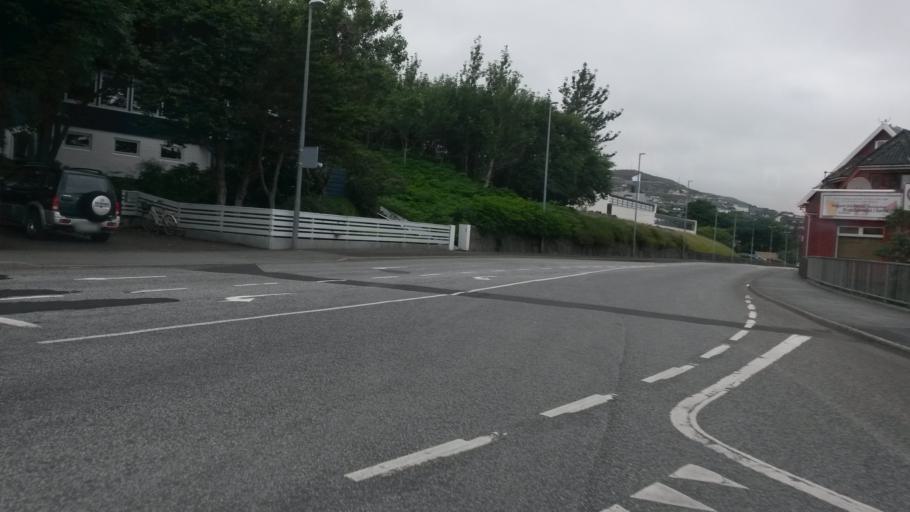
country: FO
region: Streymoy
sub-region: Torshavn
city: Torshavn
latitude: 62.0057
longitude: -6.7764
